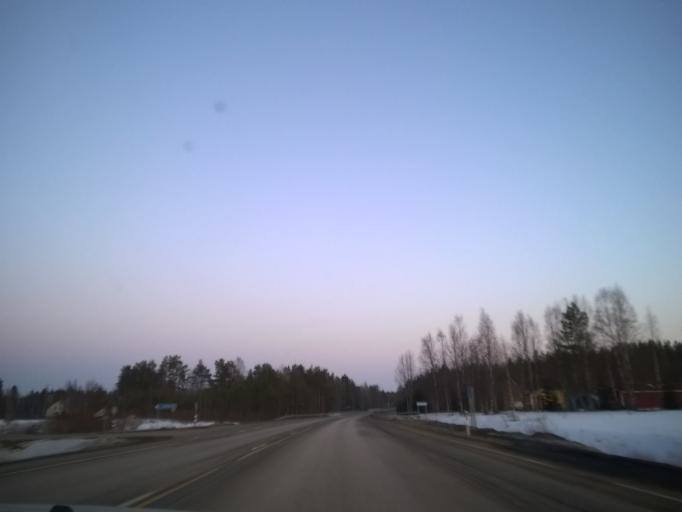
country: FI
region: Northern Ostrobothnia
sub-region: Nivala-Haapajaervi
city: Pyhaejaervi
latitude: 63.8091
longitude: 25.9104
